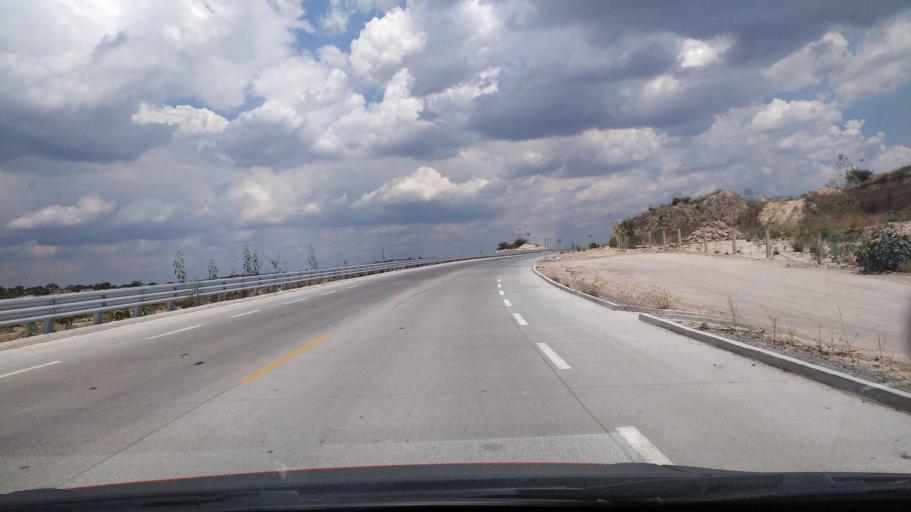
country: MX
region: Guanajuato
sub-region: Purisima del Rincon
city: Potrerillos (Guanajal)
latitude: 21.0652
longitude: -101.8717
